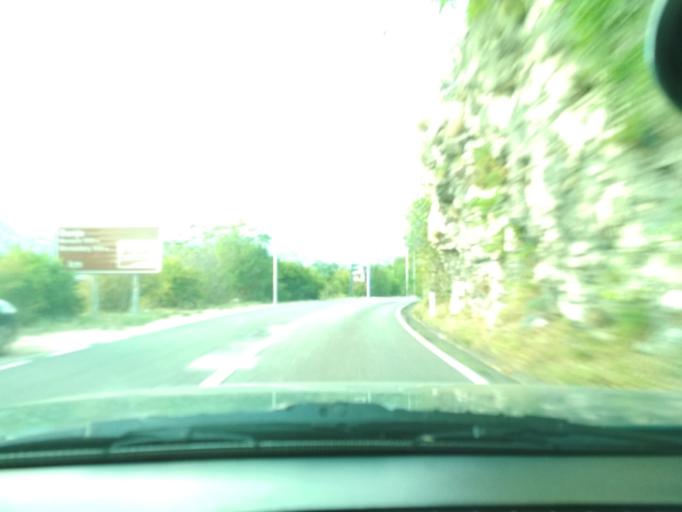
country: ME
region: Kotor
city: Risan
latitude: 42.4933
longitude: 18.6916
